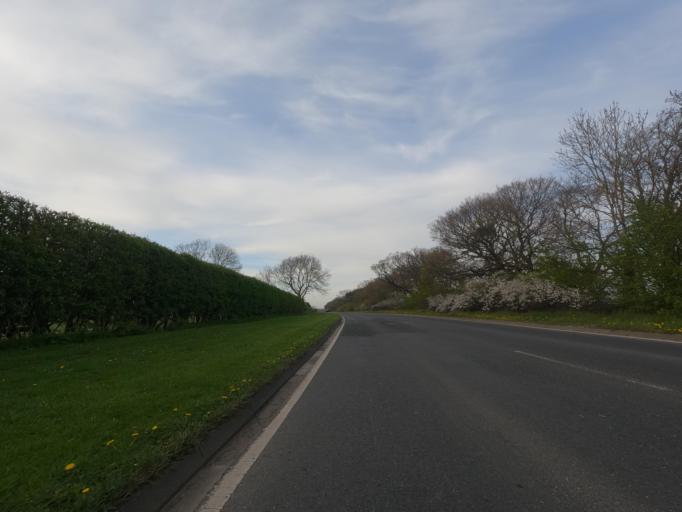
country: GB
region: England
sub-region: Newcastle upon Tyne
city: Dinnington
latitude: 55.0356
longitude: -1.6652
